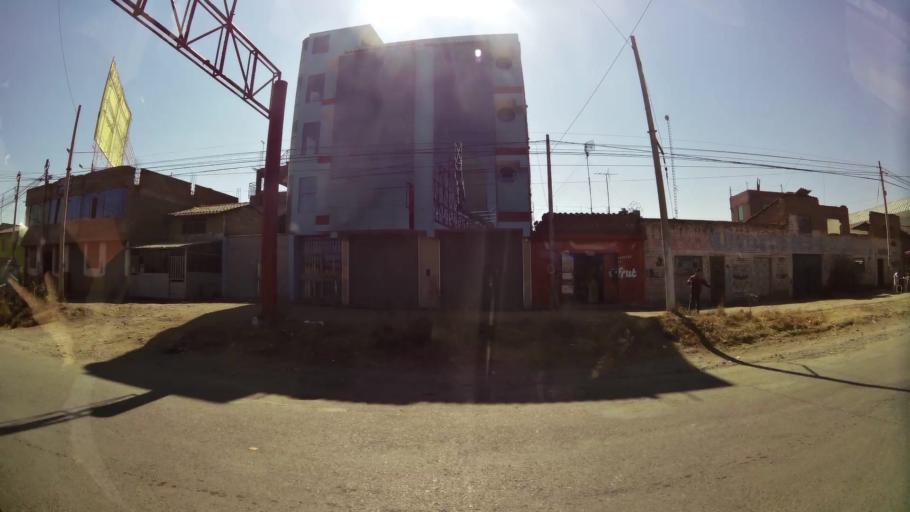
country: PE
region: Junin
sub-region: Provincia de Huancayo
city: Pilcomay
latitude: -12.0230
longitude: -75.2393
